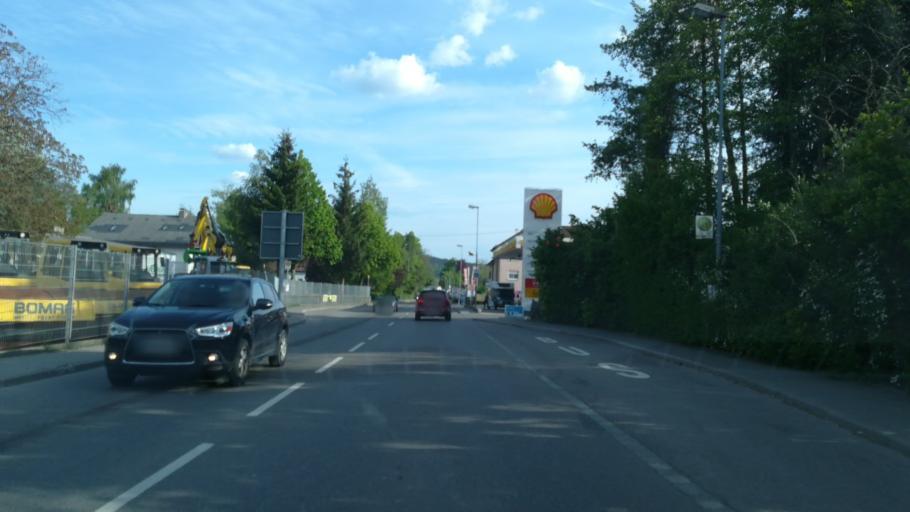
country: DE
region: Baden-Wuerttemberg
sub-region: Freiburg Region
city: Stockach
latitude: 47.8593
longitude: 9.0045
